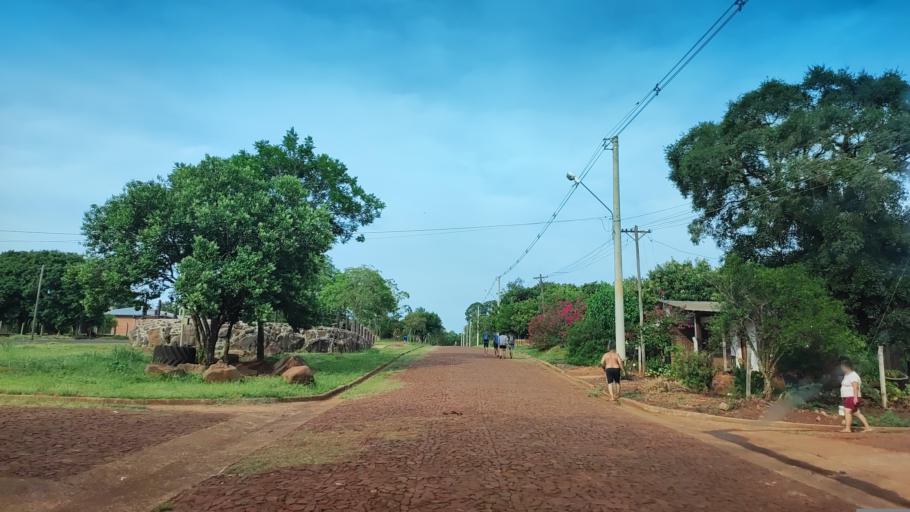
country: AR
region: Misiones
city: Gobernador Roca
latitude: -27.1328
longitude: -55.5144
